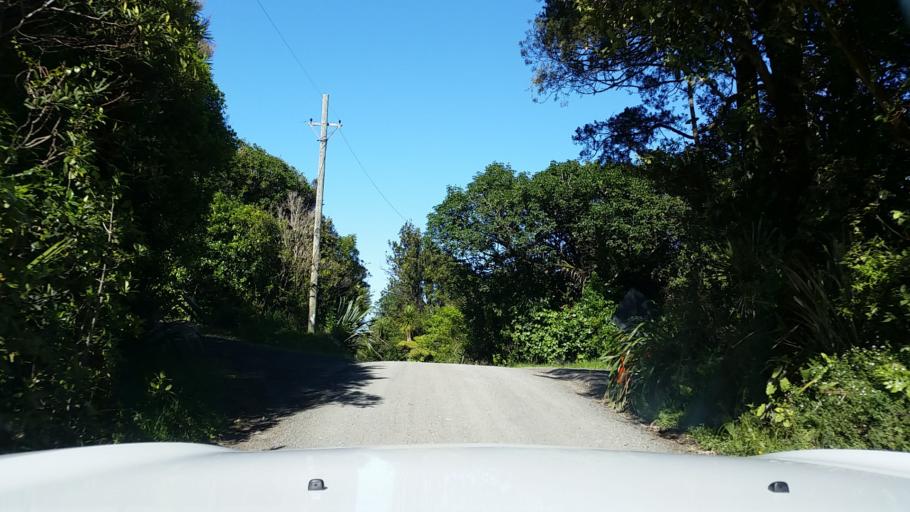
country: NZ
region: Auckland
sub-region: Auckland
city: Titirangi
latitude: -37.0268
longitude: 174.5295
